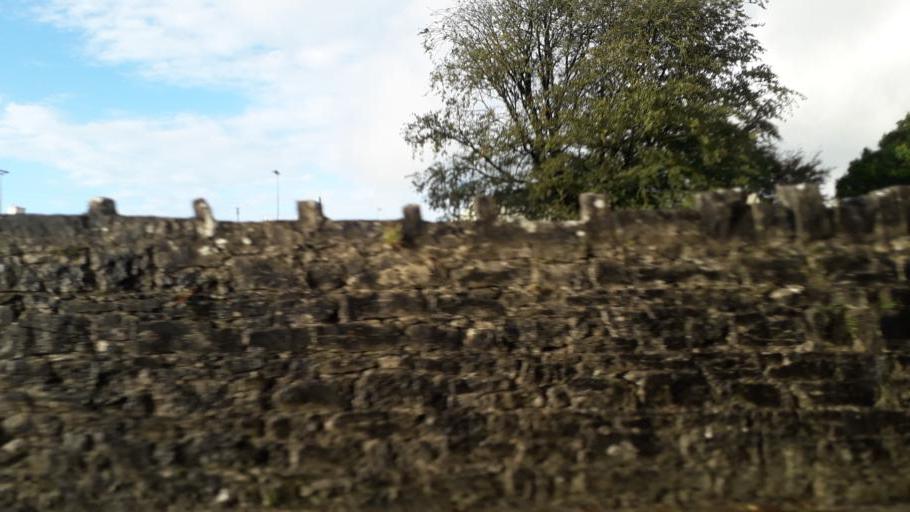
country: IE
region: Connaught
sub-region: Roscommon
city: Roscommon
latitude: 53.7766
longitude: -8.1106
